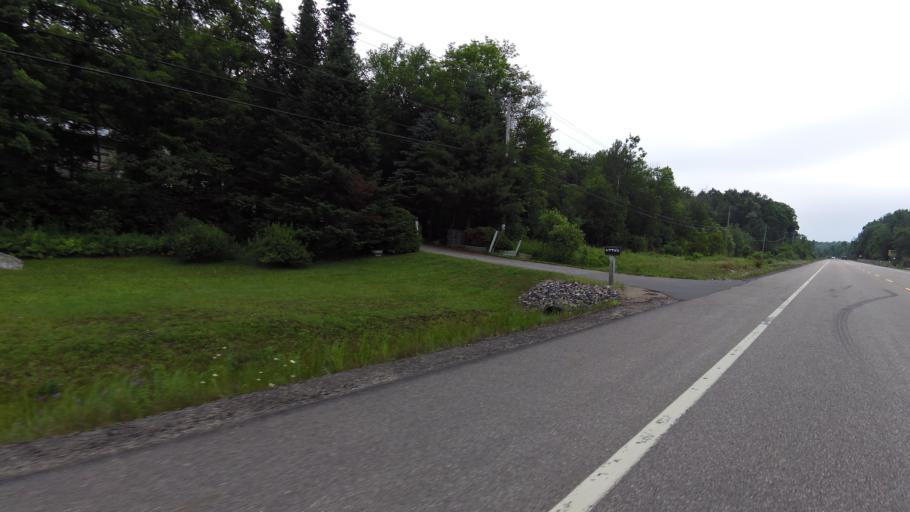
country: CA
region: Ontario
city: Huntsville
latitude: 45.3482
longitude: -78.9367
